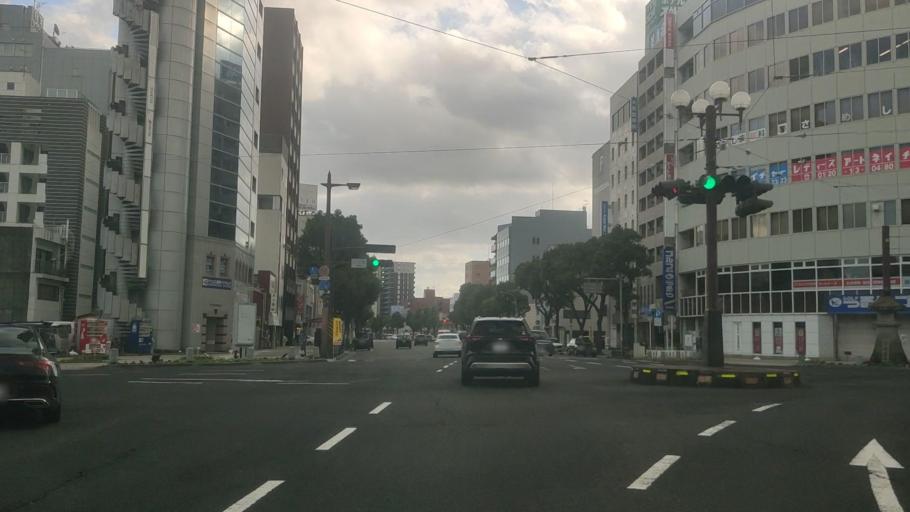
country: JP
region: Kagoshima
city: Kagoshima-shi
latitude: 31.5919
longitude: 130.5578
